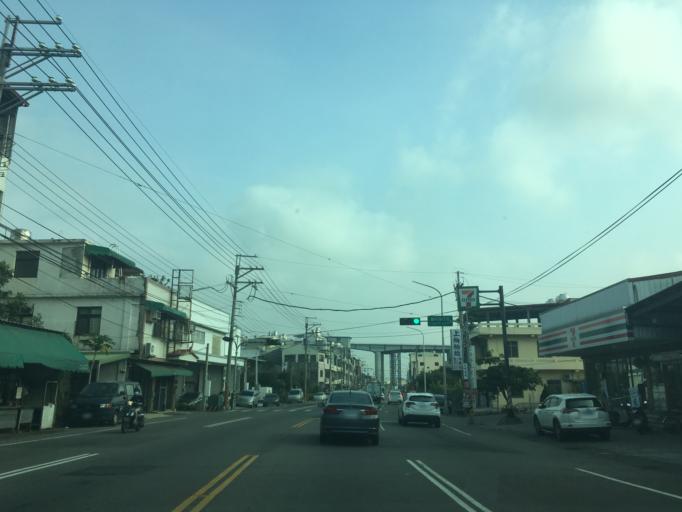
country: TW
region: Taiwan
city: Fengyuan
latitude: 24.2262
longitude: 120.7245
